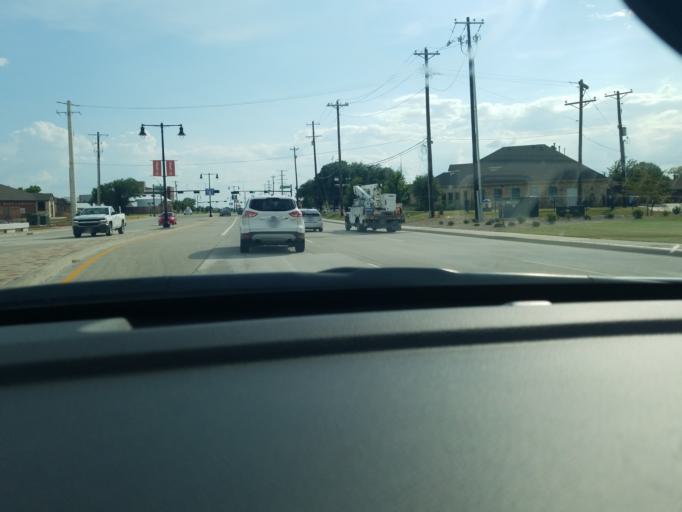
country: US
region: Texas
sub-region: Denton County
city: Little Elm
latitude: 33.1609
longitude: -96.9372
